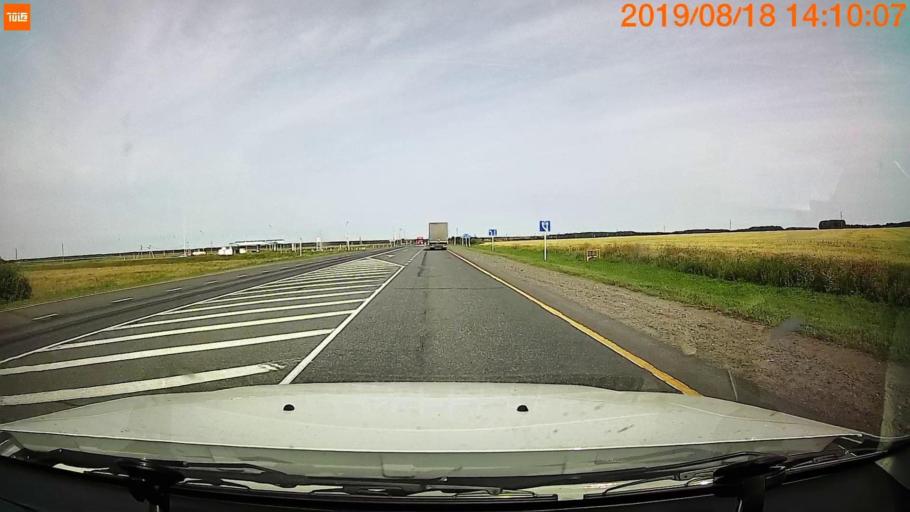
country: RU
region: Kurgan
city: Kurgan
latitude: 55.4370
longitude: 65.3558
